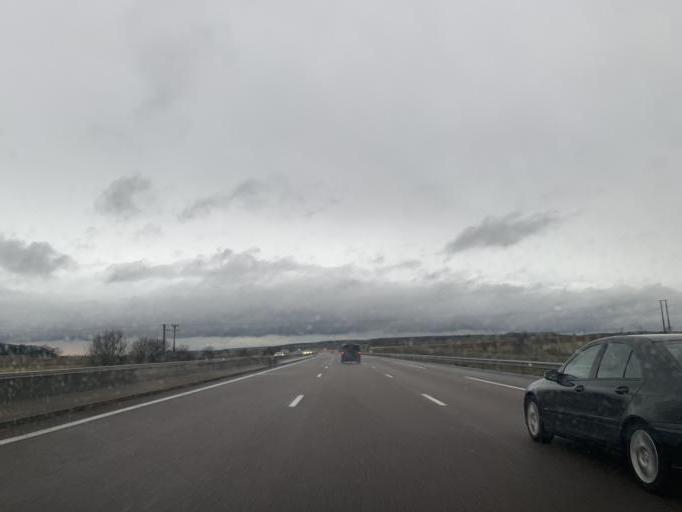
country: FR
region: Champagne-Ardenne
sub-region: Departement de la Haute-Marne
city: Rolampont
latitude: 47.8906
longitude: 5.2238
